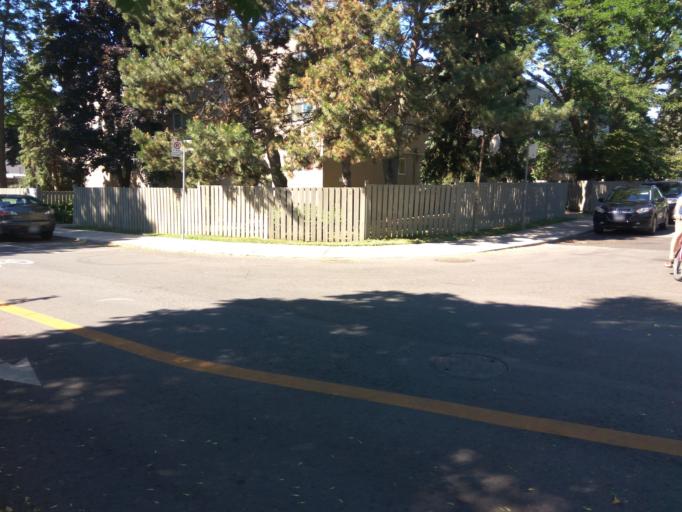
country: CA
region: Ontario
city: Toronto
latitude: 43.6497
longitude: -79.4013
